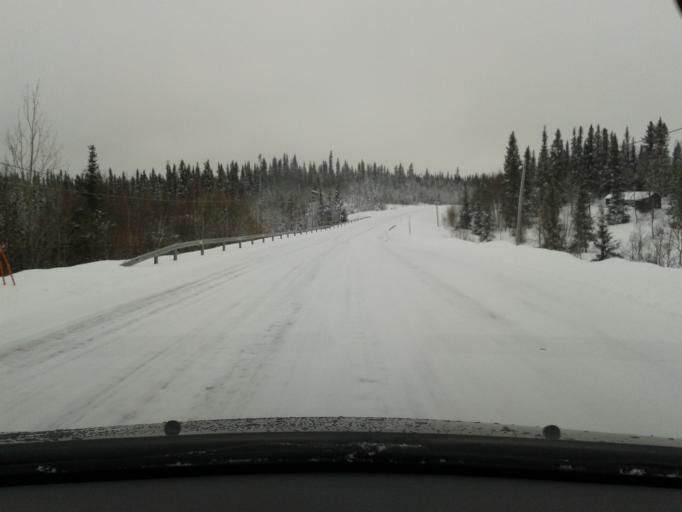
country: SE
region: Vaesterbotten
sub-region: Vilhelmina Kommun
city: Sjoberg
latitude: 65.1648
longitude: 15.8797
